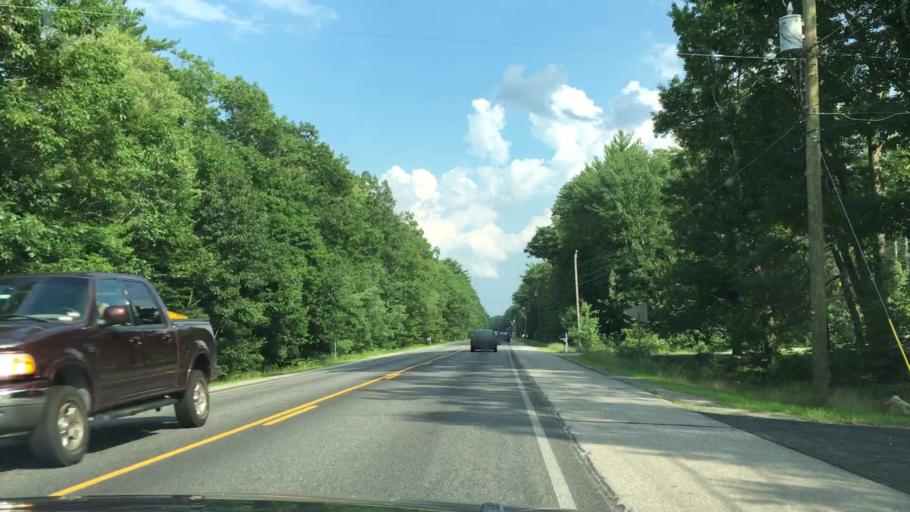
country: US
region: New Hampshire
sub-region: Strafford County
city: Farmington
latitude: 43.3965
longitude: -71.1009
